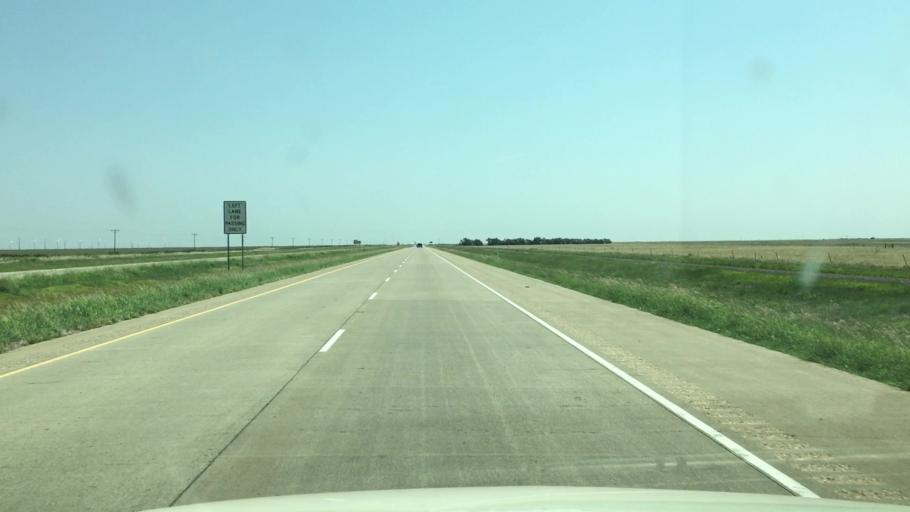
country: US
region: Texas
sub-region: Oldham County
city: Vega
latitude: 35.2655
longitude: -102.5405
